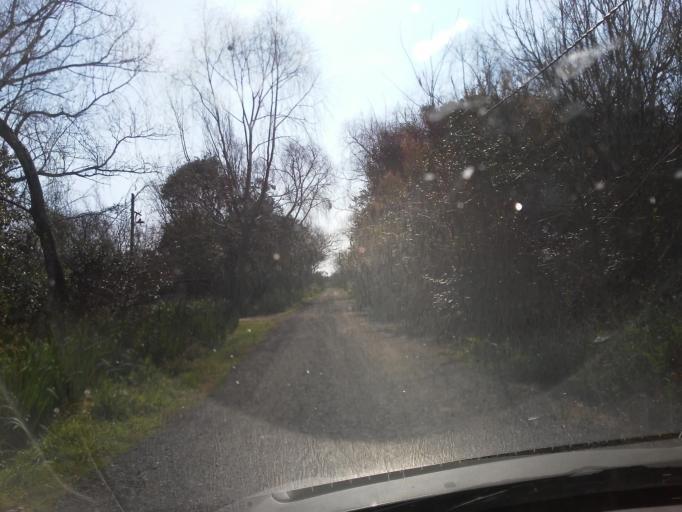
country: AR
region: Buenos Aires
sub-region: Partido de Avellaneda
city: Avellaneda
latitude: -34.6700
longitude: -58.3097
